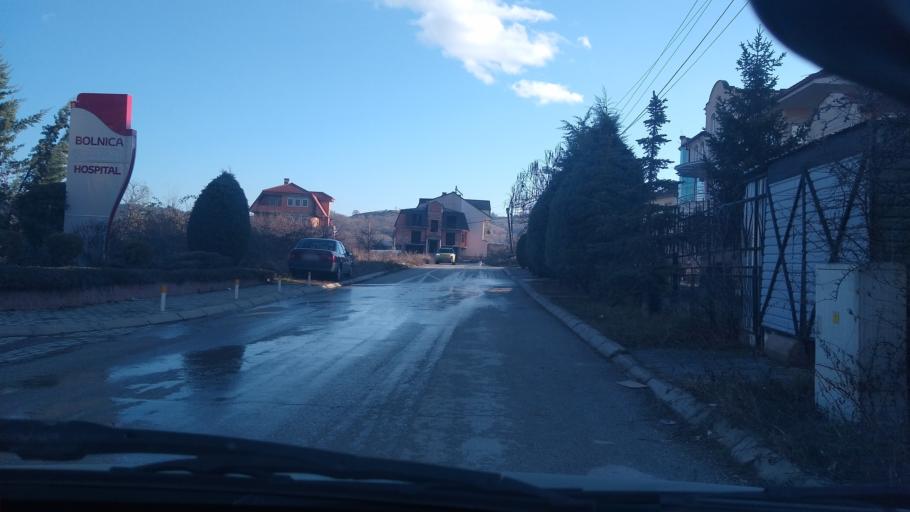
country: MK
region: Bitola
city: Bitola
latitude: 41.0209
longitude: 21.3158
